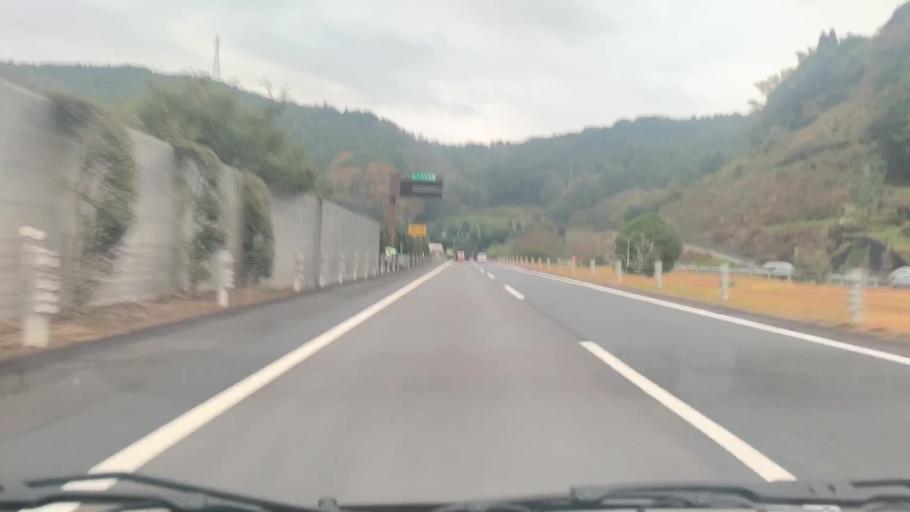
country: JP
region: Nagasaki
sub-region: Isahaya-shi
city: Isahaya
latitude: 32.8763
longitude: 129.9974
